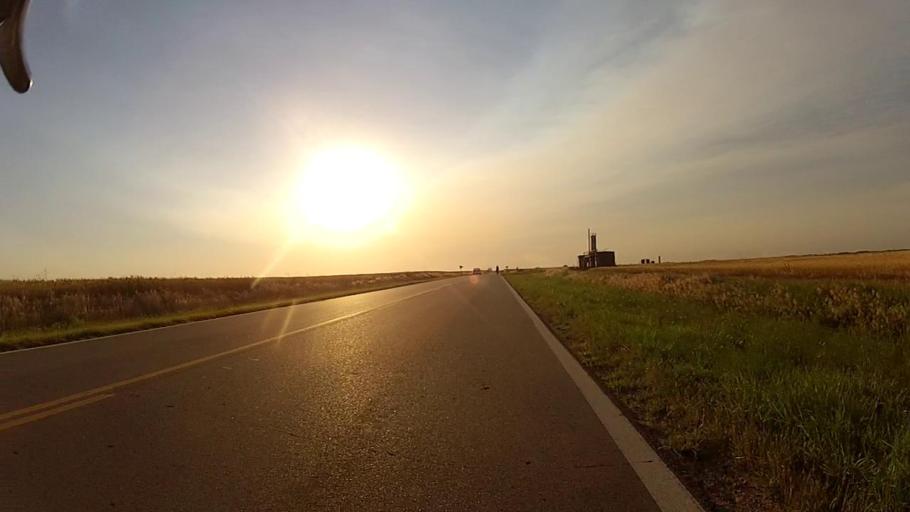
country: US
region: Kansas
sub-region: Harper County
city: Anthony
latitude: 37.1533
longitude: -97.9160
